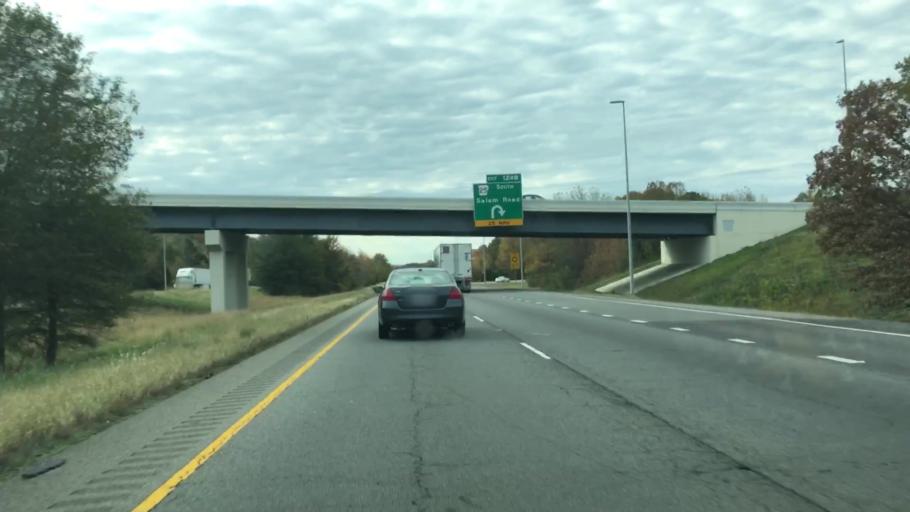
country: US
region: Arkansas
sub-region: Faulkner County
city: Conway
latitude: 35.1191
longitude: -92.4593
